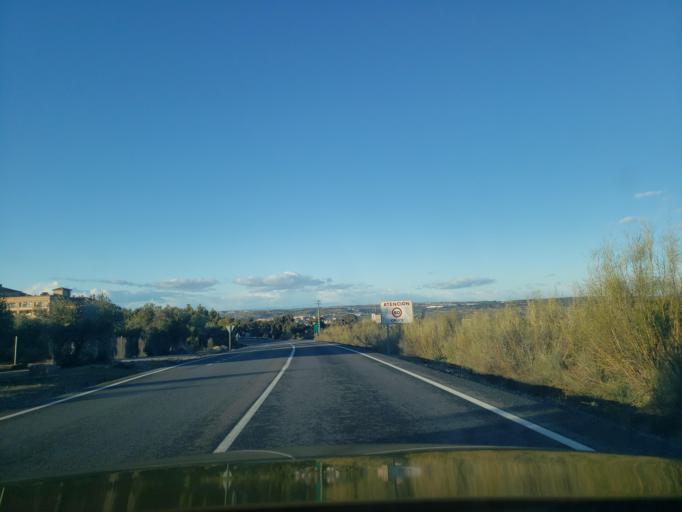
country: ES
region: Castille-La Mancha
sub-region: Province of Toledo
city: Toledo
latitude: 39.8417
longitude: -4.0190
